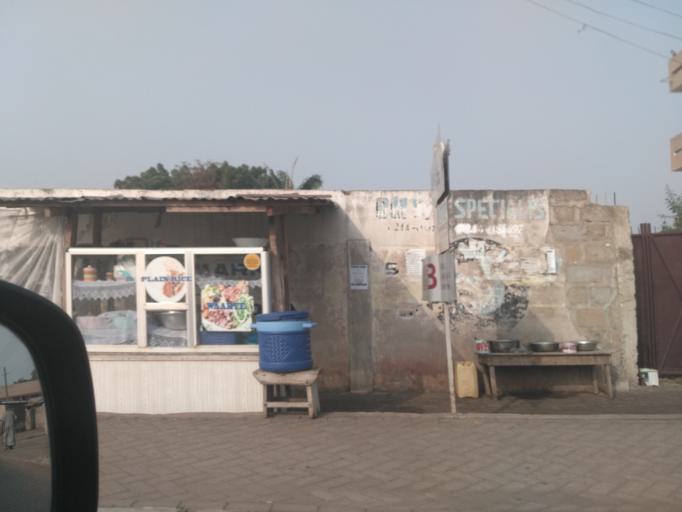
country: GH
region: Greater Accra
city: Accra
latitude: 5.5758
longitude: -0.2008
